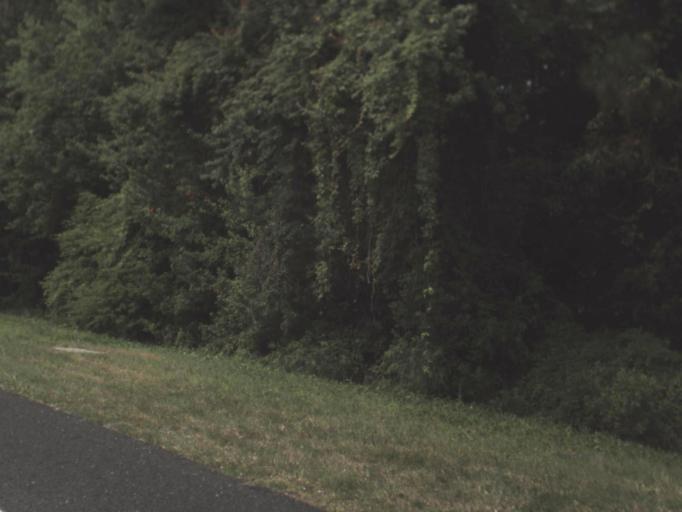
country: US
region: Florida
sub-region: Clay County
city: Orange Park
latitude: 30.1236
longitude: -81.7045
